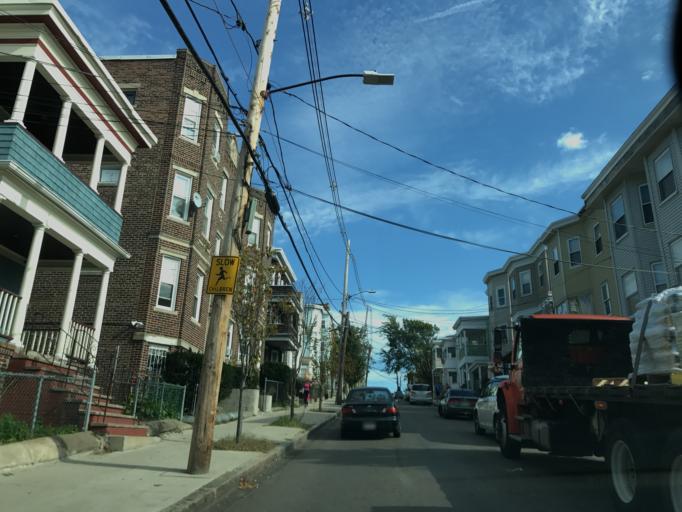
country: US
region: Massachusetts
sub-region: Suffolk County
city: Chelsea
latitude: 42.3921
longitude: -71.0317
